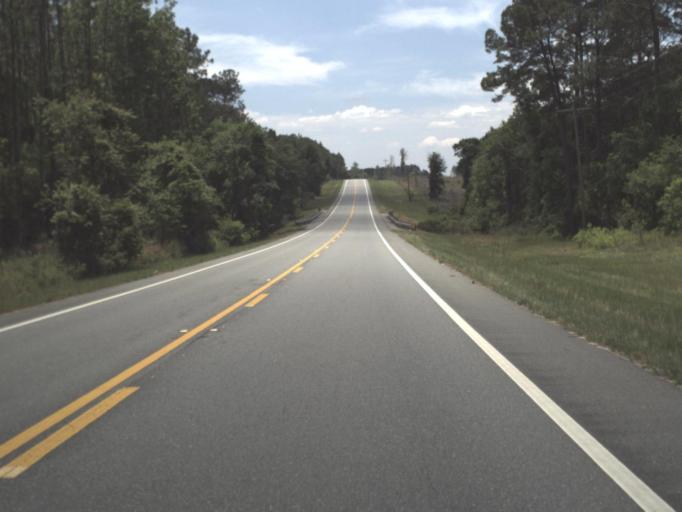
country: US
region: Florida
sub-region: Gulf County
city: Wewahitchka
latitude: 30.2752
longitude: -85.1622
